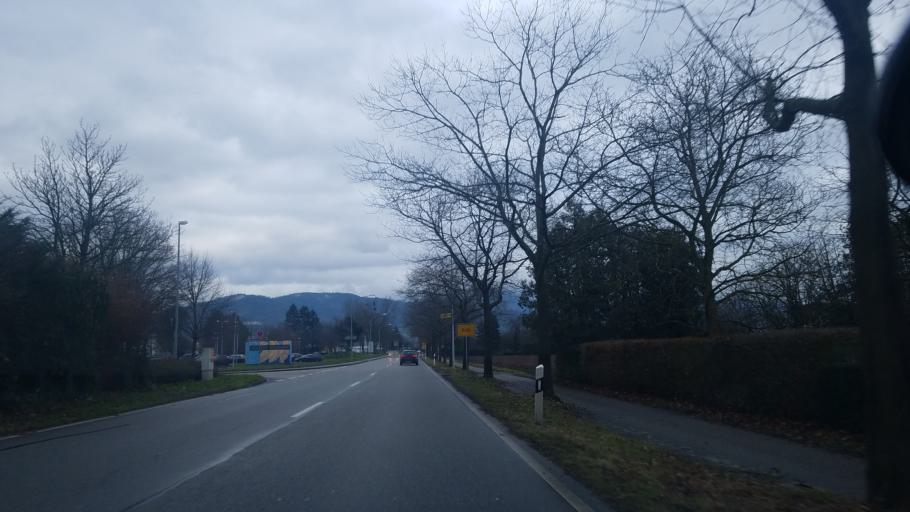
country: DE
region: Baden-Wuerttemberg
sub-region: Karlsruhe Region
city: Buhl
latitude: 48.7066
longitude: 8.1212
